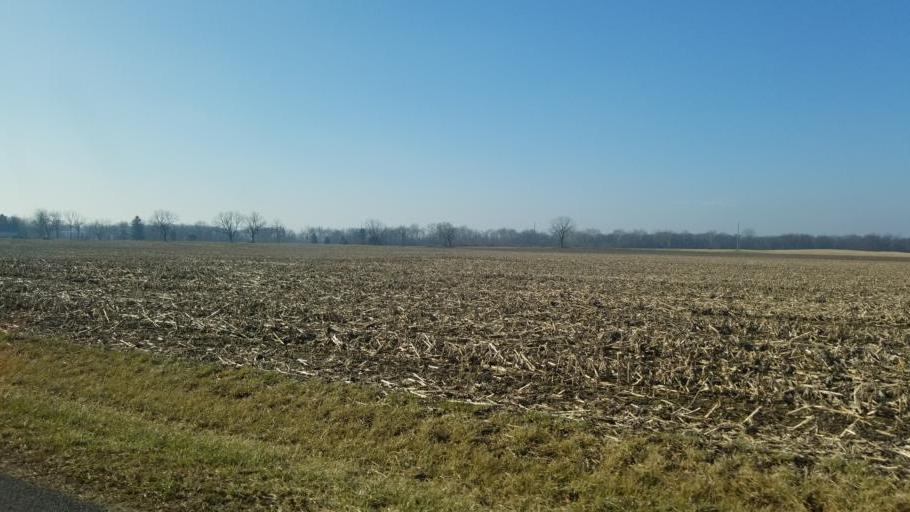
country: US
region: Ohio
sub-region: Seneca County
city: Tiffin
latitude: 41.0704
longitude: -83.1127
